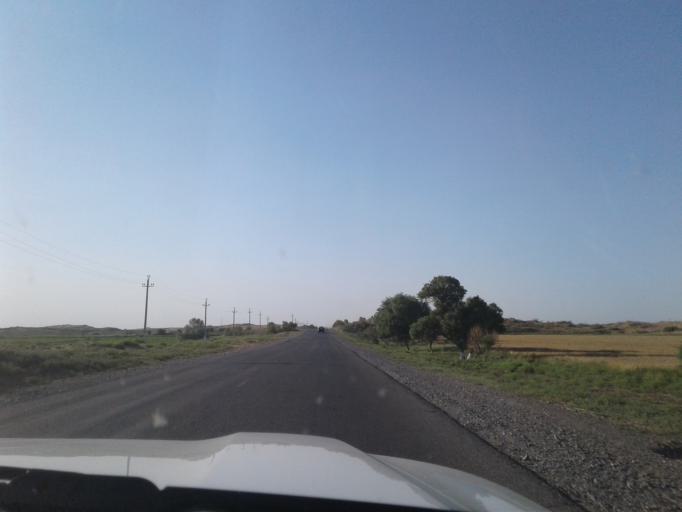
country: TM
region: Mary
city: Yoloeten
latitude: 37.2473
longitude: 62.3675
